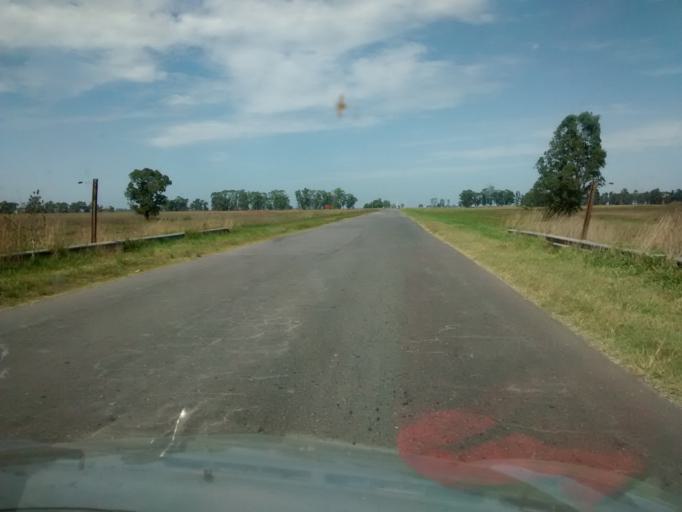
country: AR
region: Buenos Aires
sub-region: Partido de Ayacucho
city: Ayacucho
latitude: -37.2192
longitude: -58.4990
